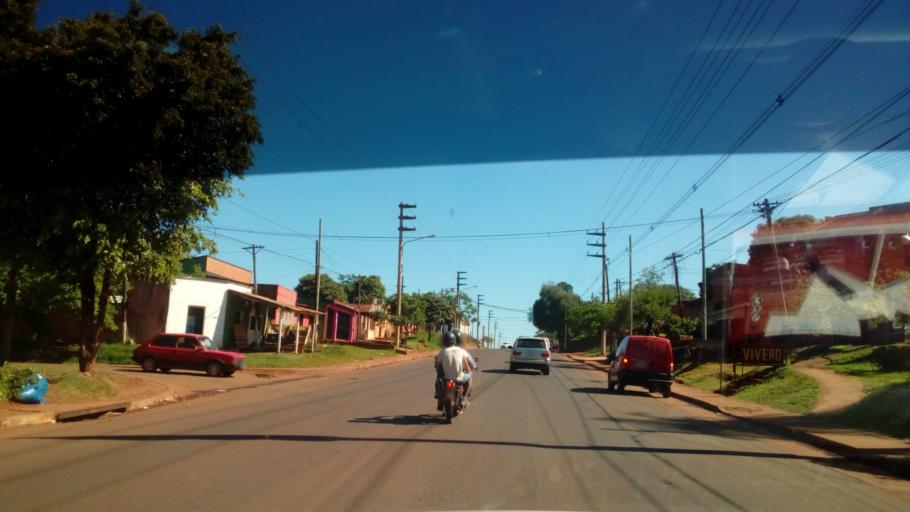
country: AR
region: Misiones
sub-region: Departamento de Capital
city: Posadas
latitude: -27.4122
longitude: -55.9122
